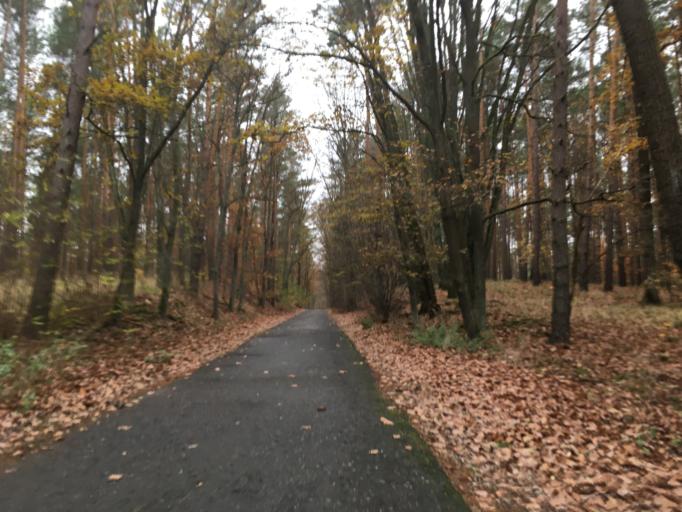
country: DE
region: Brandenburg
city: Mixdorf
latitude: 52.1711
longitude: 14.4411
